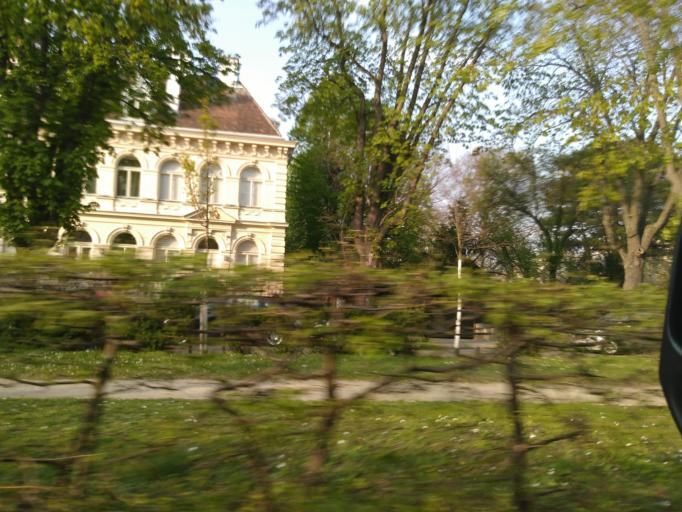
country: AT
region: Lower Austria
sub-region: Politischer Bezirk Modling
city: Perchtoldsdorf
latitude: 48.1815
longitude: 16.2959
